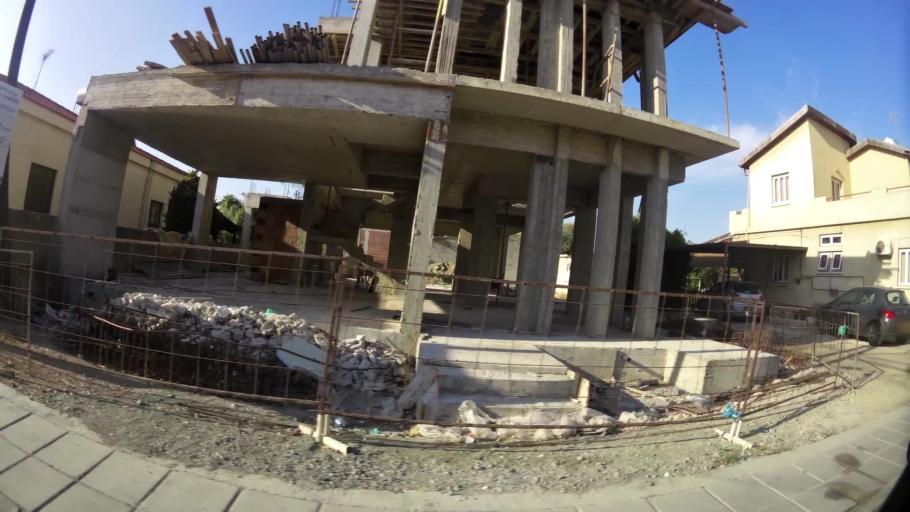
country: CY
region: Larnaka
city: Aradippou
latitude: 34.9411
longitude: 33.5925
